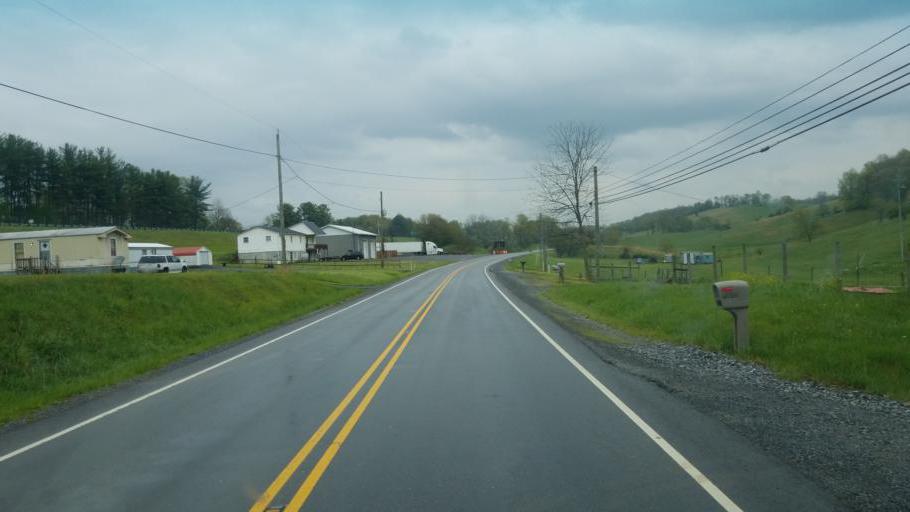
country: US
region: Virginia
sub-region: Wythe County
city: Rural Retreat
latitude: 36.8987
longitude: -81.3315
